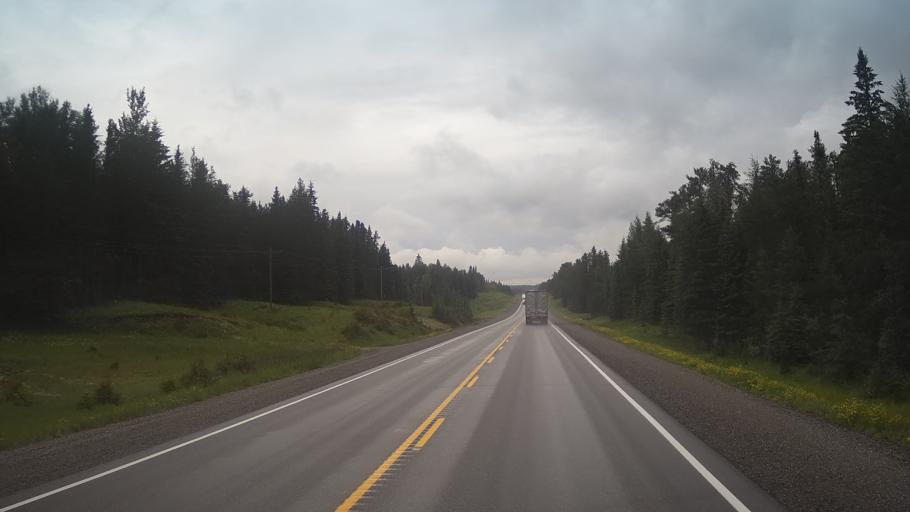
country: CA
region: Ontario
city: Neebing
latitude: 48.6525
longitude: -89.8930
